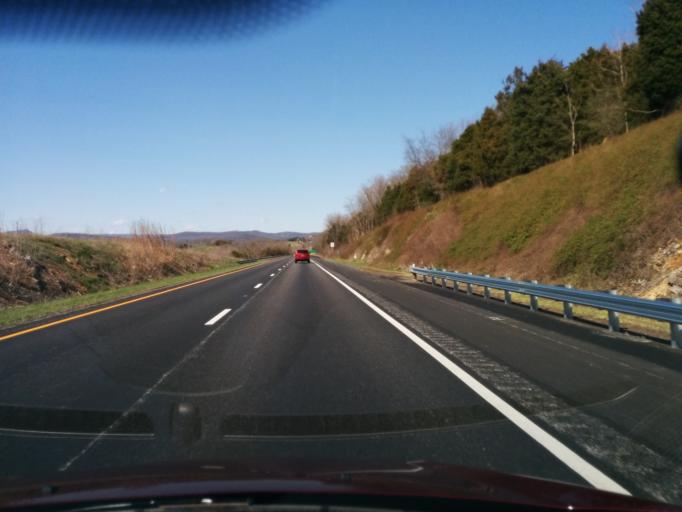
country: US
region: Virginia
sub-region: Rockbridge County
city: East Lexington
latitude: 37.7649
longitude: -79.4056
